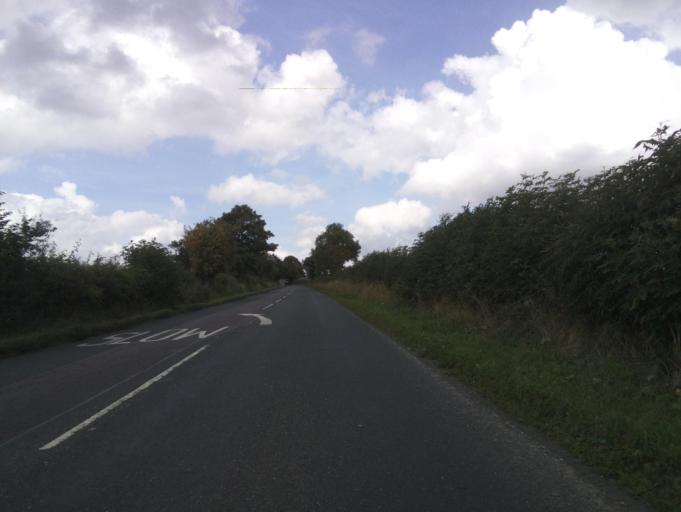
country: GB
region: England
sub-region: North Yorkshire
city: Catterick Garrison
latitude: 54.4272
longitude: -1.6823
